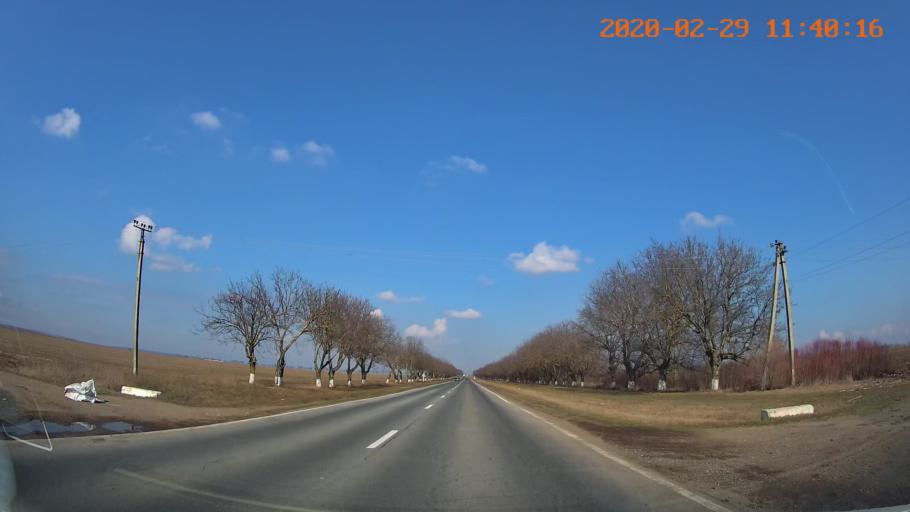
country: MD
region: Rezina
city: Saharna
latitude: 47.6537
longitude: 29.0209
